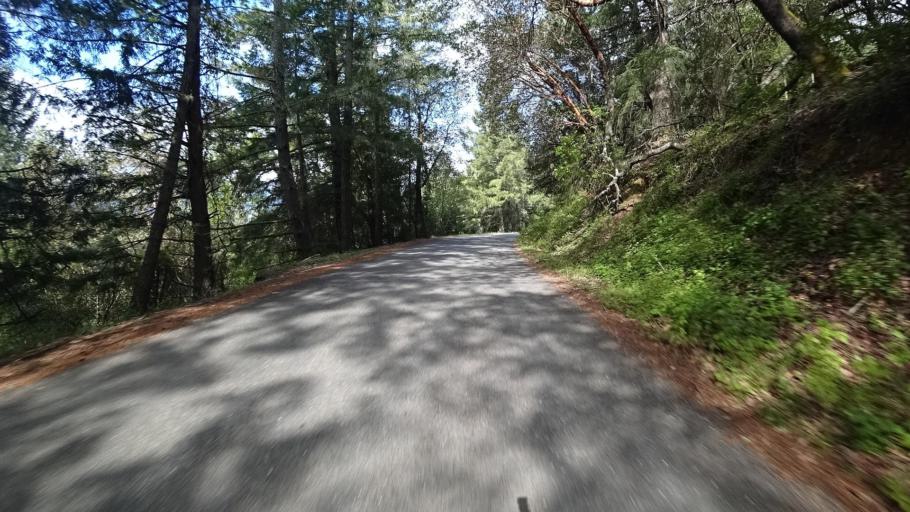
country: US
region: California
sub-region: Humboldt County
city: Redway
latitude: 40.1708
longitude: -123.5667
